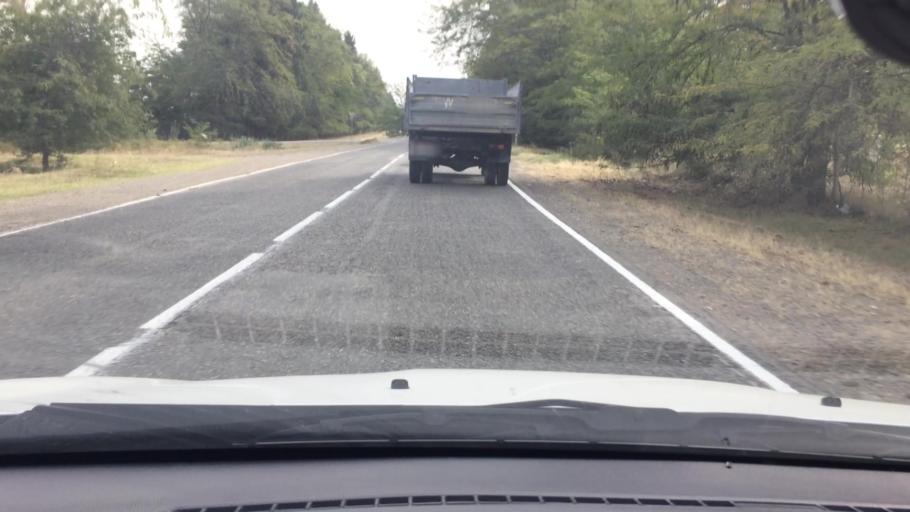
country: GE
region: Kvemo Kartli
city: Rust'avi
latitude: 41.4705
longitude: 44.9794
